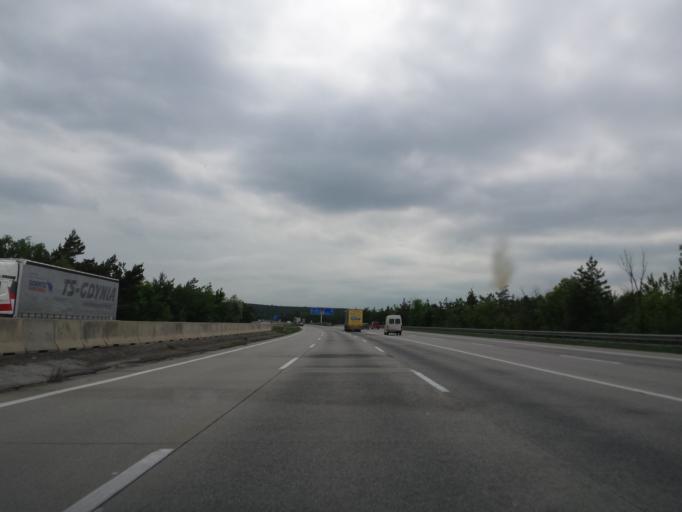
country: AT
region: Lower Austria
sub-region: Politischer Bezirk Neunkirchen
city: Breitenau
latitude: 47.7194
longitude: 16.1359
